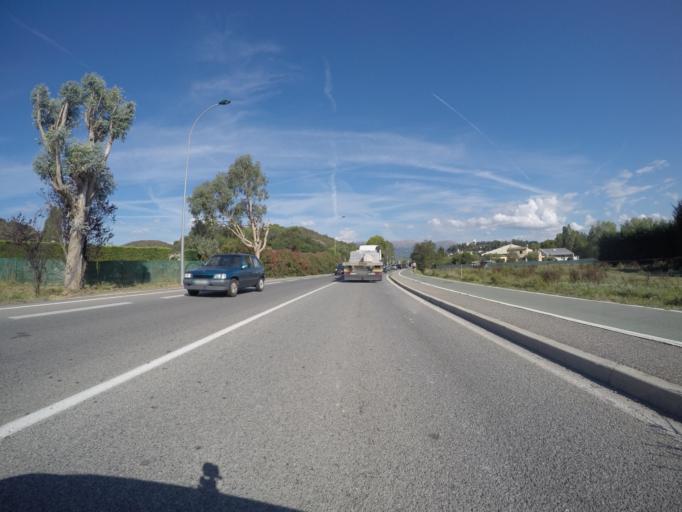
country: FR
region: Provence-Alpes-Cote d'Azur
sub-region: Departement des Alpes-Maritimes
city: Villeneuve-Loubet
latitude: 43.6503
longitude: 7.1302
